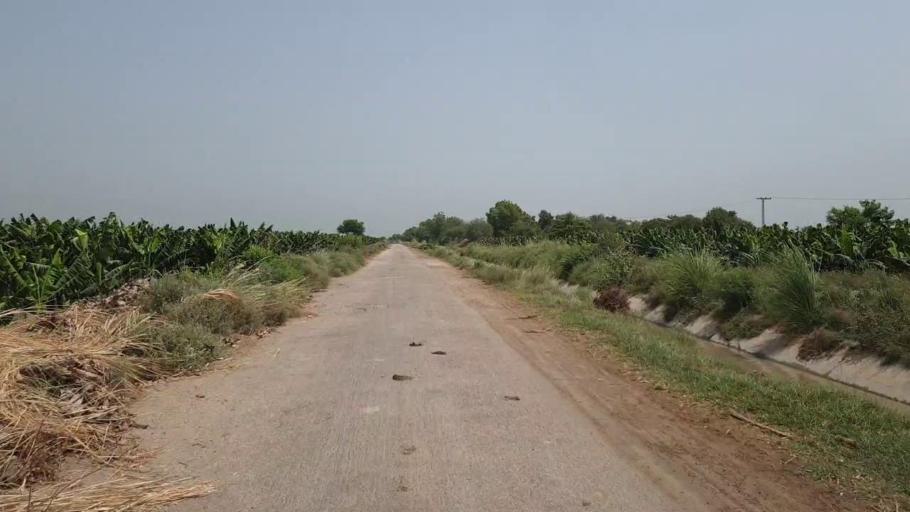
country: PK
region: Sindh
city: Nawabshah
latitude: 26.2848
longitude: 68.3106
